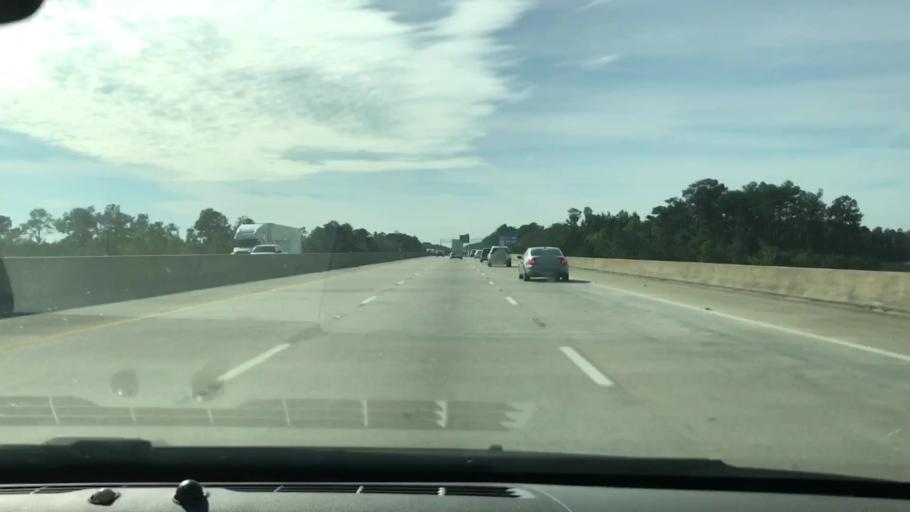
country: US
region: Mississippi
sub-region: Hancock County
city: Diamondhead
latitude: 30.3634
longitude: -89.4073
